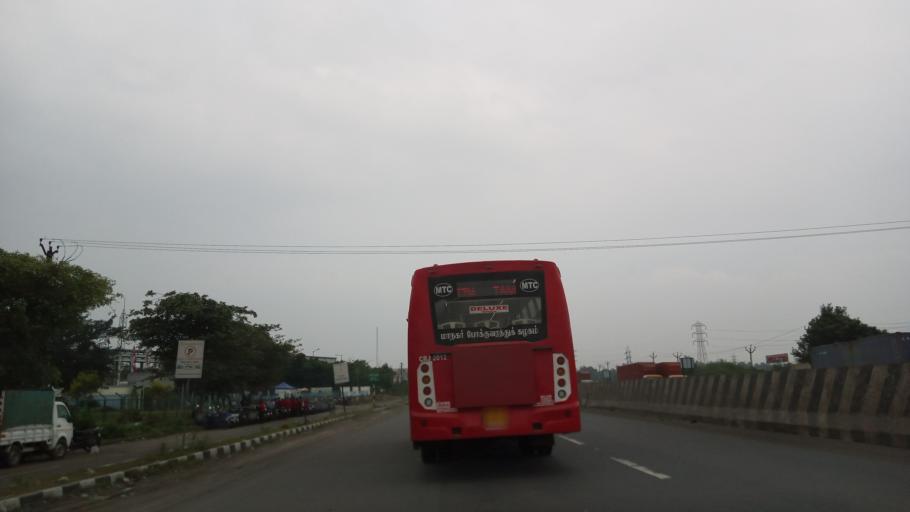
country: IN
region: Tamil Nadu
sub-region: Kancheepuram
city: Madambakkam
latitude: 12.8532
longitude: 79.9462
